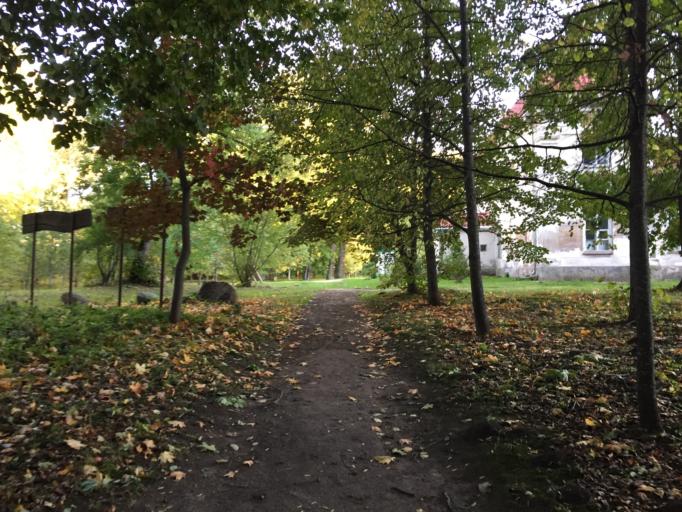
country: LV
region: Varaklani
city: Varaklani
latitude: 56.6082
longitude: 26.7768
